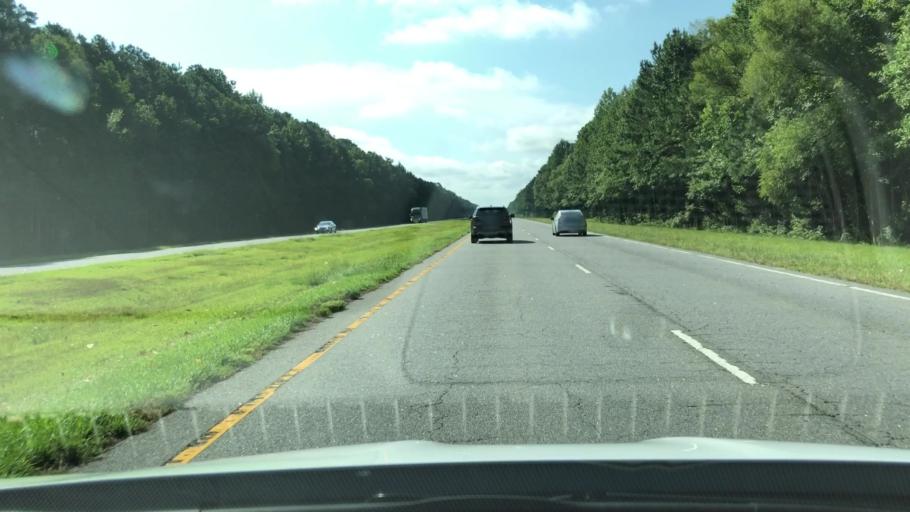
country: US
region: North Carolina
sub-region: Pasquotank County
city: Elizabeth City
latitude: 36.3988
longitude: -76.3305
